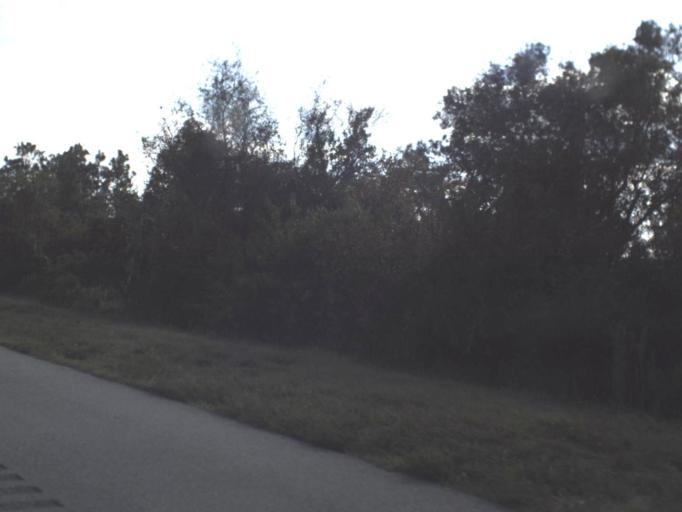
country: US
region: Florida
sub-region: Osceola County
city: Saint Cloud
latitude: 28.0976
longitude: -81.2769
